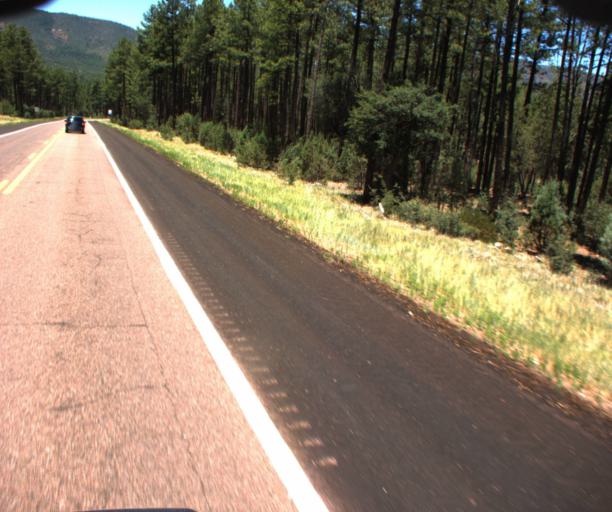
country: US
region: Arizona
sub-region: Gila County
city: Pine
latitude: 34.3698
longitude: -111.4407
